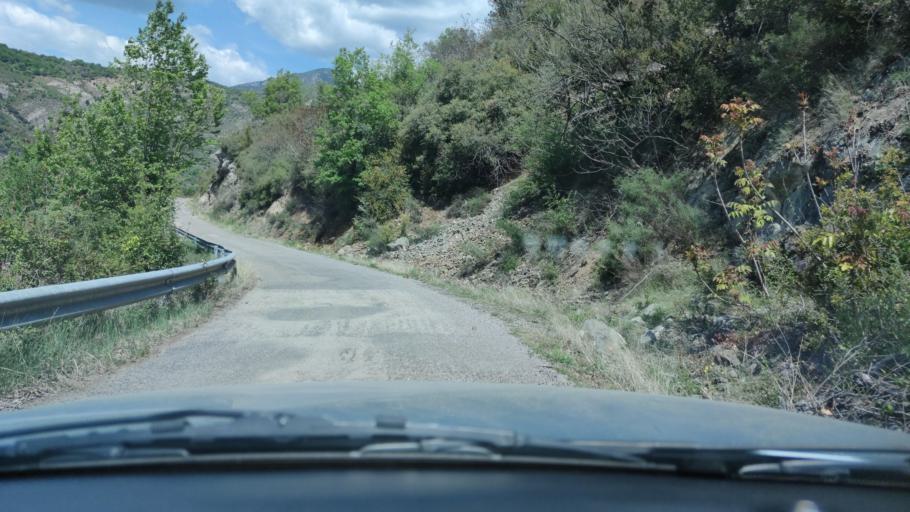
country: ES
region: Catalonia
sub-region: Provincia de Lleida
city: Sort
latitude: 42.3144
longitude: 1.0656
